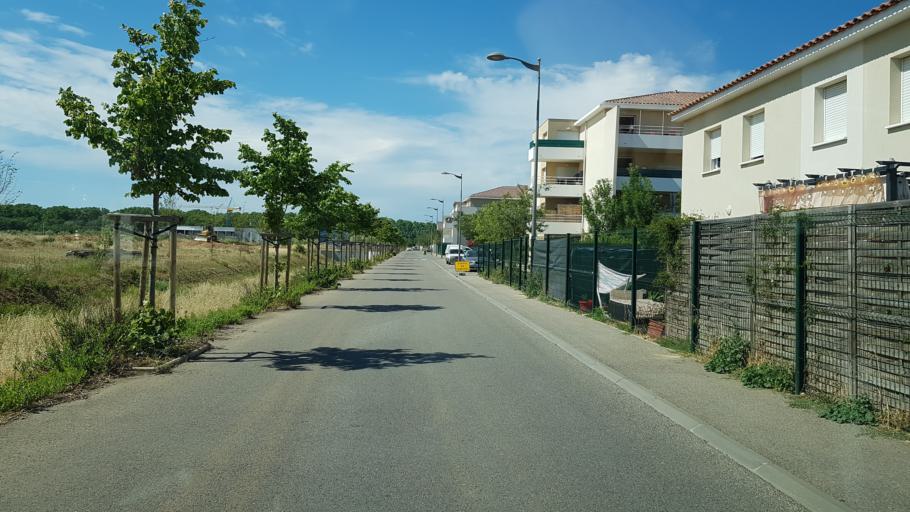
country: FR
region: Provence-Alpes-Cote d'Azur
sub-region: Departement des Bouches-du-Rhone
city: Saint-Martin-de-Crau
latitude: 43.6374
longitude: 4.7954
